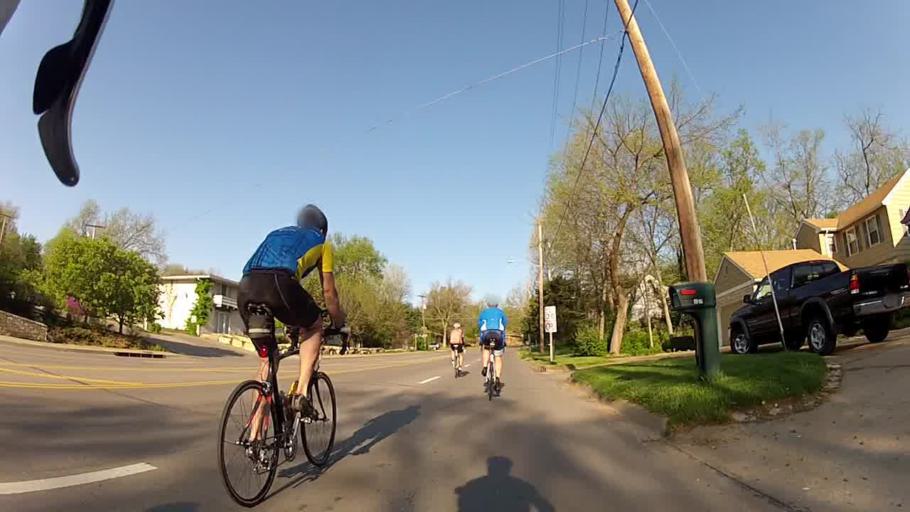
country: US
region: Kansas
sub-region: Riley County
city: Manhattan
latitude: 39.1860
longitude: -96.5896
